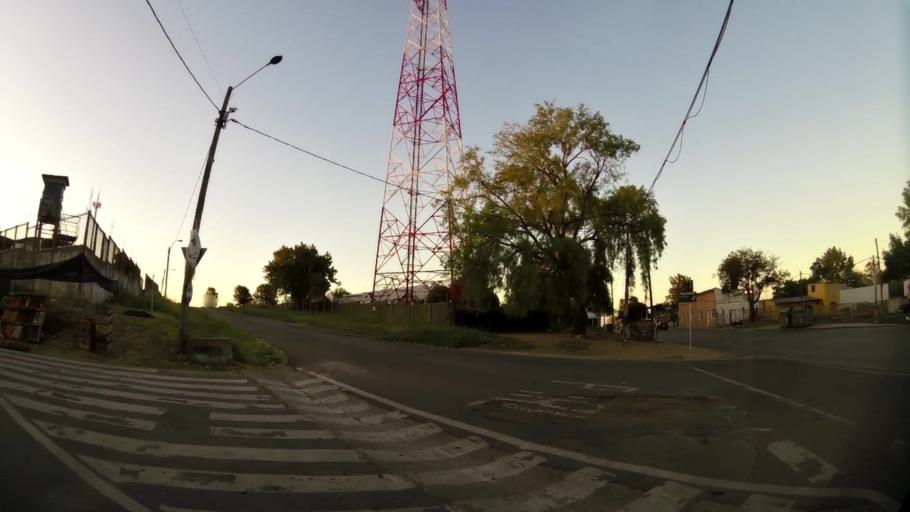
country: UY
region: Montevideo
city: Montevideo
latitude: -34.8288
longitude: -56.1547
